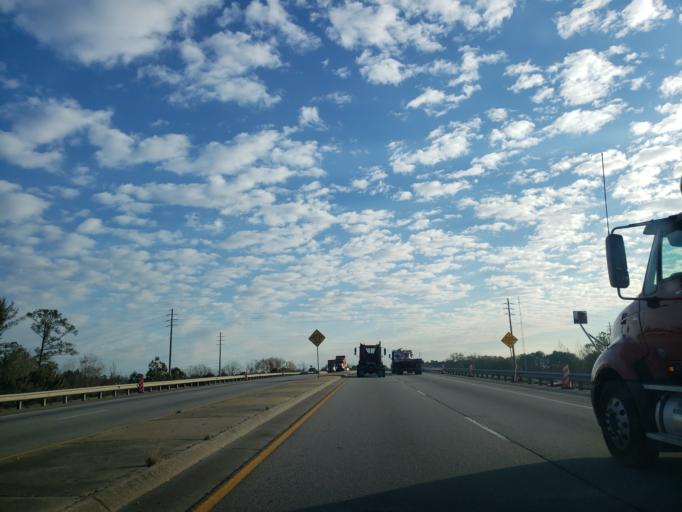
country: US
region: Georgia
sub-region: Chatham County
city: Port Wentworth
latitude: 32.1633
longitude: -81.1868
